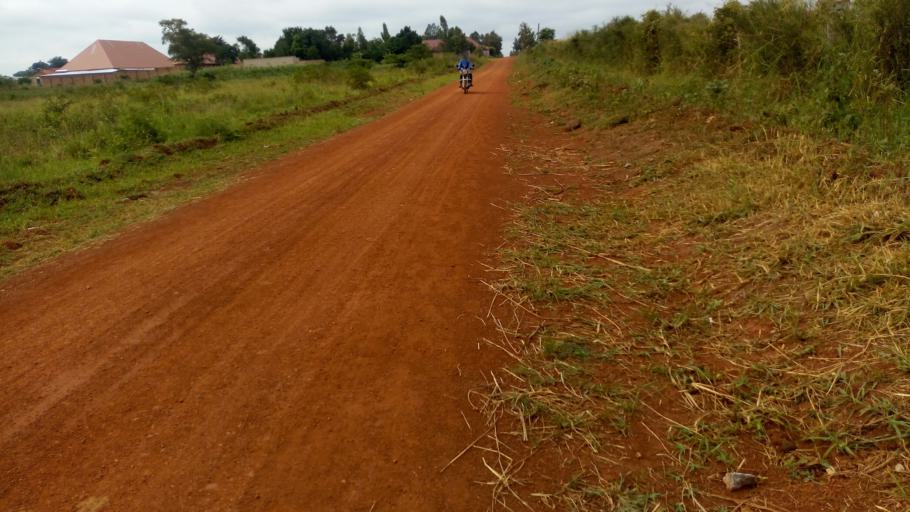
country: UG
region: Western Region
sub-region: Kiryandongo District
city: Kiryandongo
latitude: 1.8060
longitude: 32.0136
